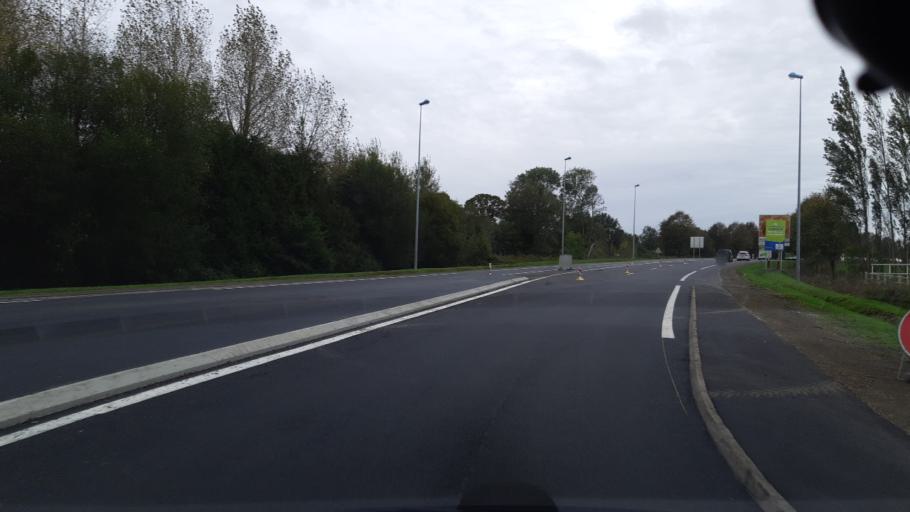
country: FR
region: Lower Normandy
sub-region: Departement de la Manche
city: Brehal
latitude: 48.9013
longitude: -1.5007
